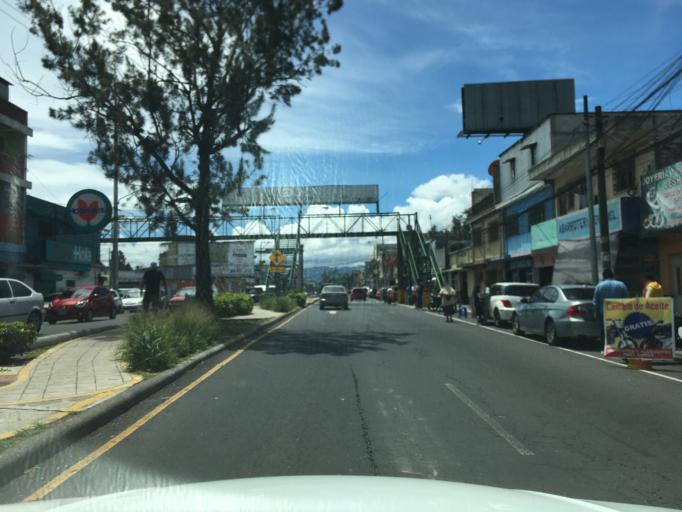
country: GT
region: Guatemala
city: Guatemala City
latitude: 14.6263
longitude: -90.5432
